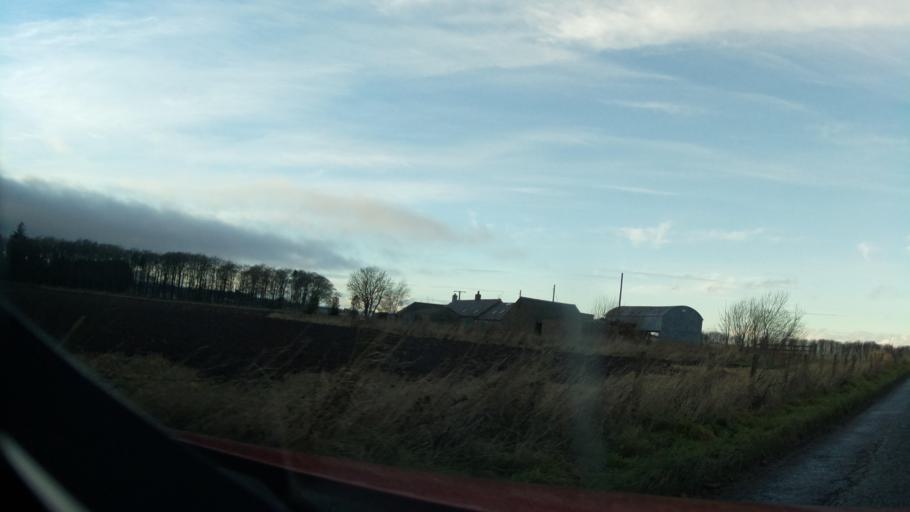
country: GB
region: Scotland
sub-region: Angus
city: Letham
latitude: 56.5611
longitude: -2.7713
